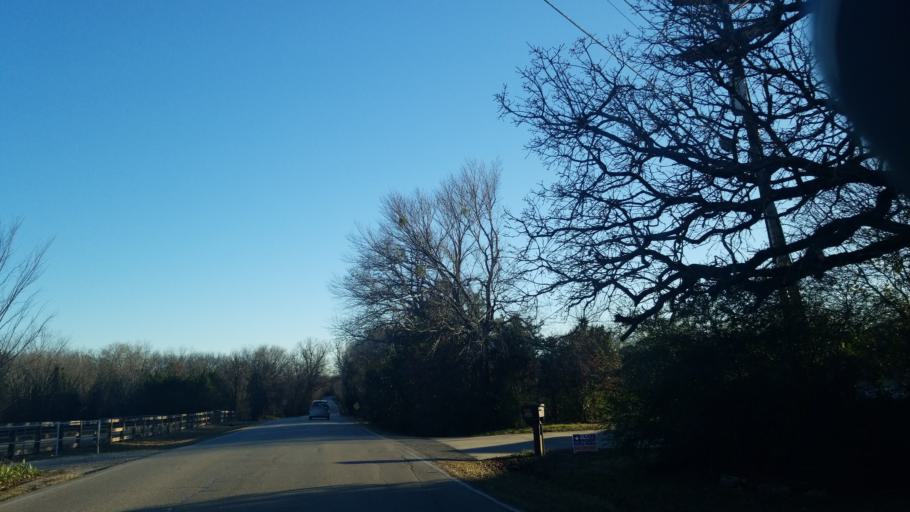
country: US
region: Texas
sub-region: Denton County
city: Shady Shores
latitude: 33.1564
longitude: -97.0293
